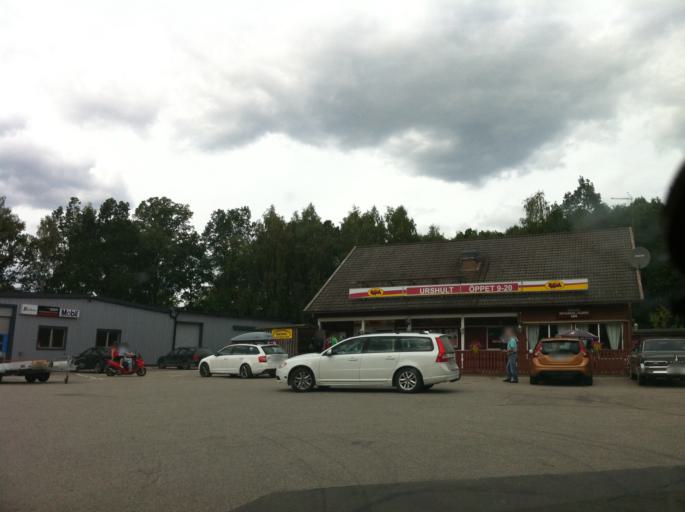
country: SE
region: Kronoberg
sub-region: Tingsryds Kommun
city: Tingsryd
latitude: 56.5294
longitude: 14.8205
